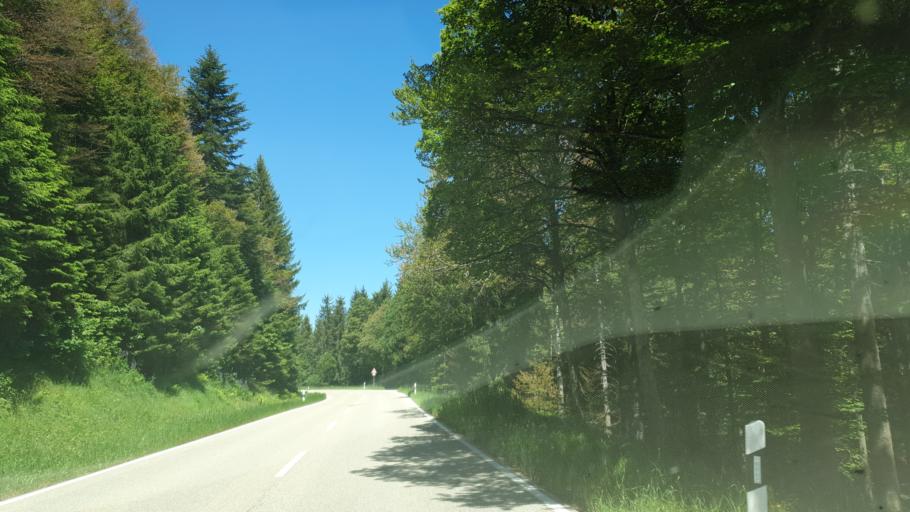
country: DE
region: Baden-Wuerttemberg
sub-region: Freiburg Region
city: Wieden
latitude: 47.8815
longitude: 7.9011
